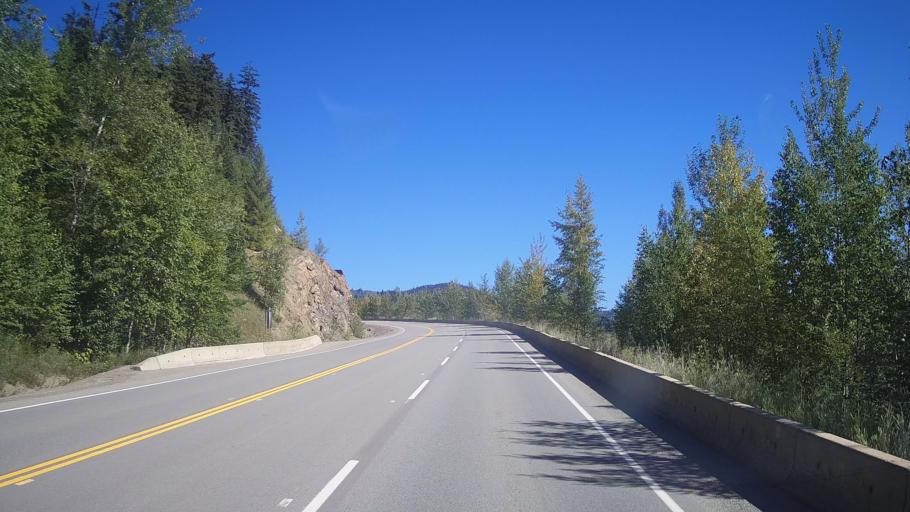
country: CA
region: British Columbia
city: Kamloops
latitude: 51.4756
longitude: -120.2576
